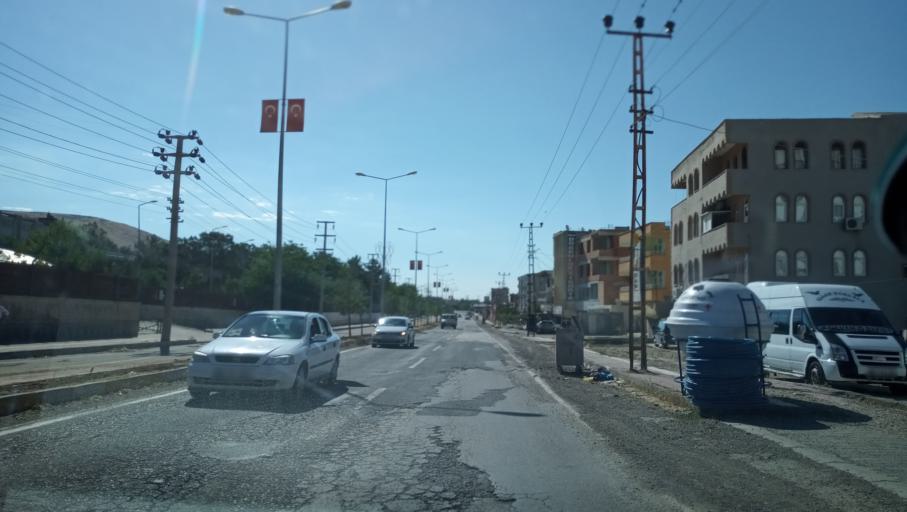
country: TR
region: Diyarbakir
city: Silvan
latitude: 38.1374
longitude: 41.0216
